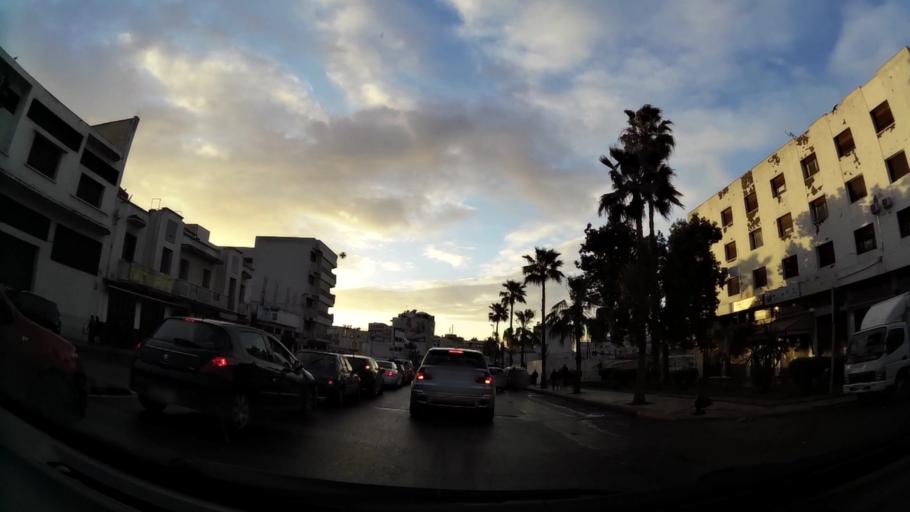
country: MA
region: Grand Casablanca
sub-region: Casablanca
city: Casablanca
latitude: 33.5832
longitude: -7.6040
